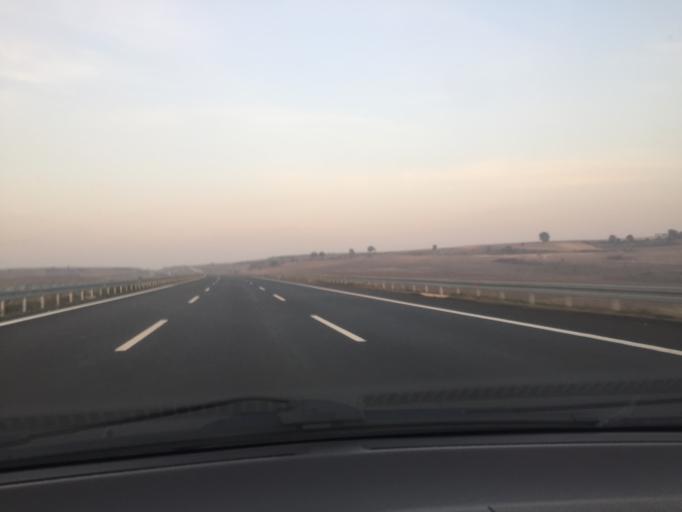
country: TR
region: Bursa
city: Mahmudiye
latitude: 40.2684
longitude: 28.6353
